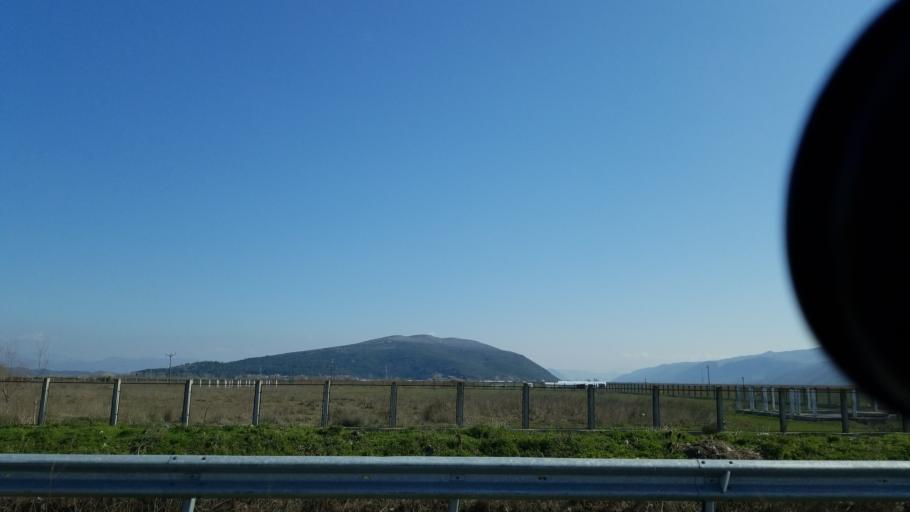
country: AL
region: Shkoder
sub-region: Rrethi i Shkodres
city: Dajc
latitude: 41.9408
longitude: 19.4447
